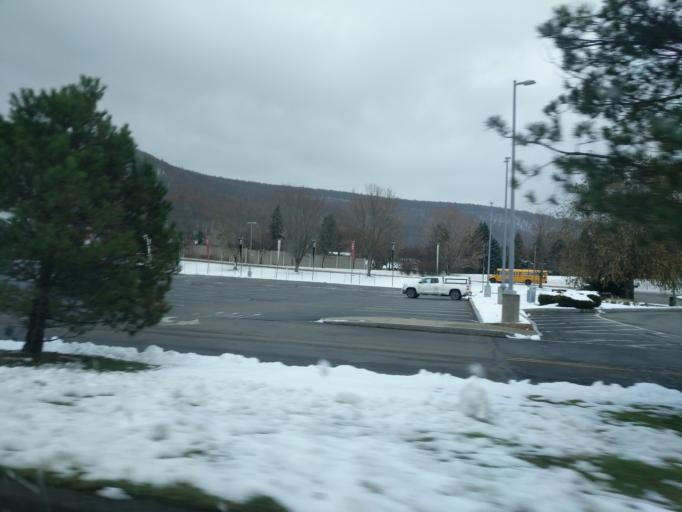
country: US
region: New York
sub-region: Steuben County
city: Corning
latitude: 42.1532
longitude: -77.0546
